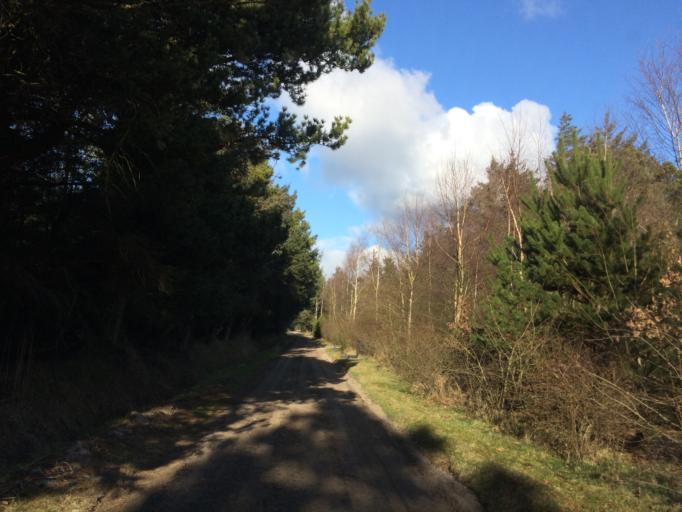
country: DK
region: Central Jutland
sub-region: Holstebro Kommune
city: Ulfborg
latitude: 56.2642
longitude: 8.1449
